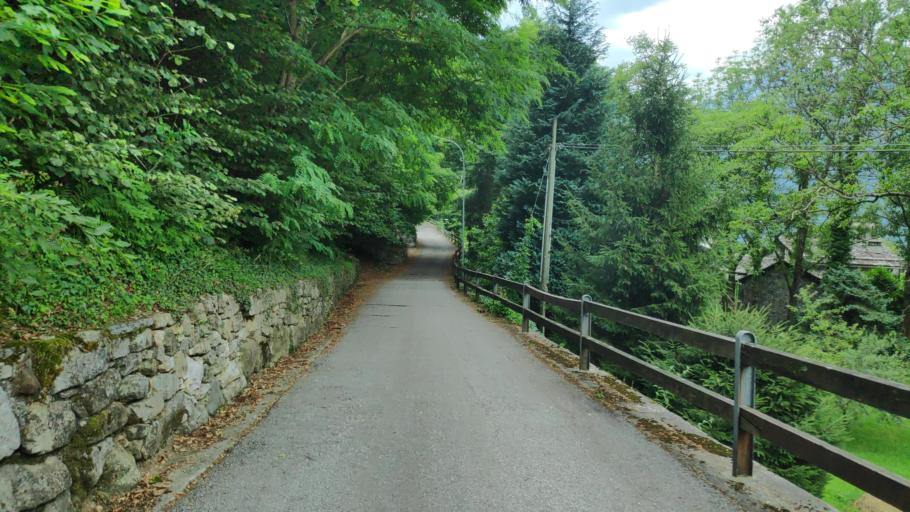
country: IT
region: Lombardy
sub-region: Provincia di Sondrio
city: Prata Camportaccio
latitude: 46.3023
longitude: 9.3994
